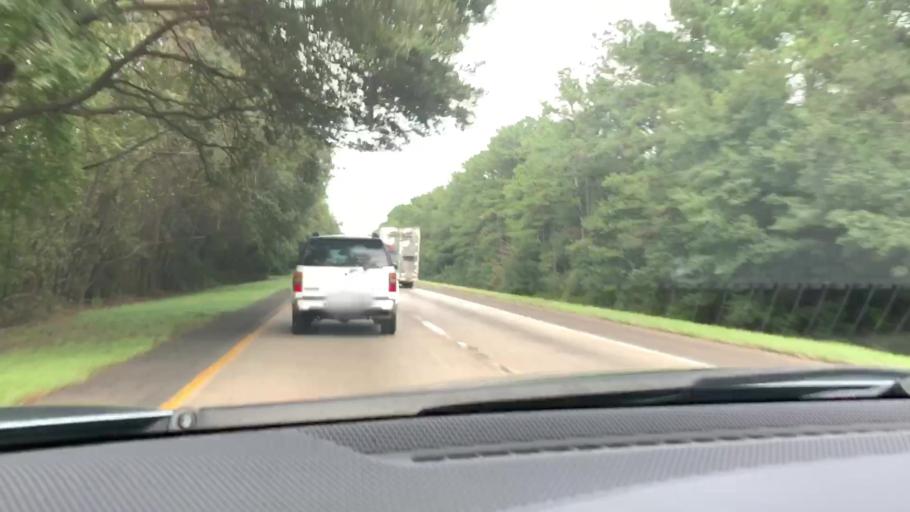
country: US
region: South Carolina
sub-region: Hampton County
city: Yemassee
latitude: 32.7748
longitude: -80.7982
